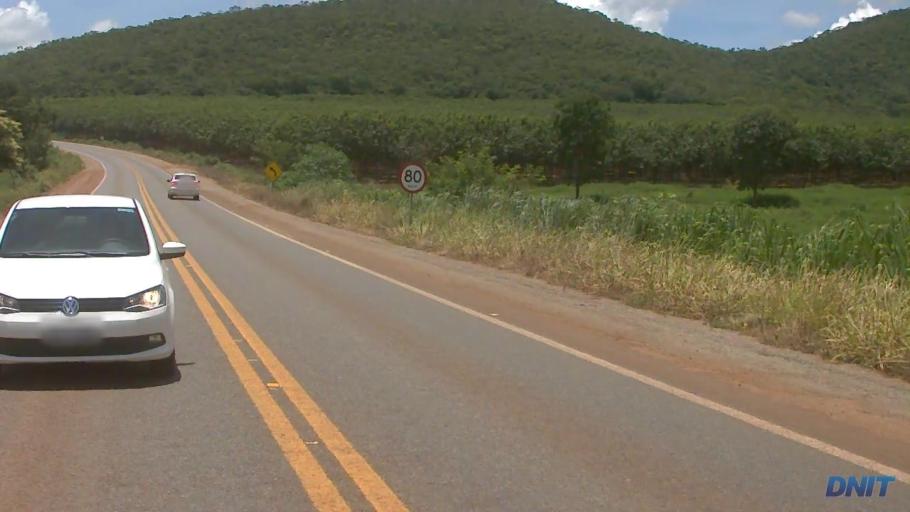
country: BR
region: Goias
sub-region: Barro Alto
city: Barro Alto
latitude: -14.9850
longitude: -48.9233
